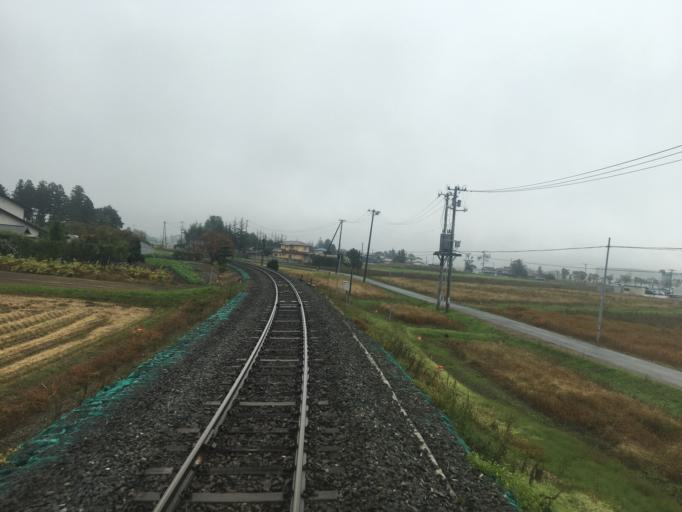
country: JP
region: Miyagi
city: Furukawa
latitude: 38.5753
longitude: 140.8985
